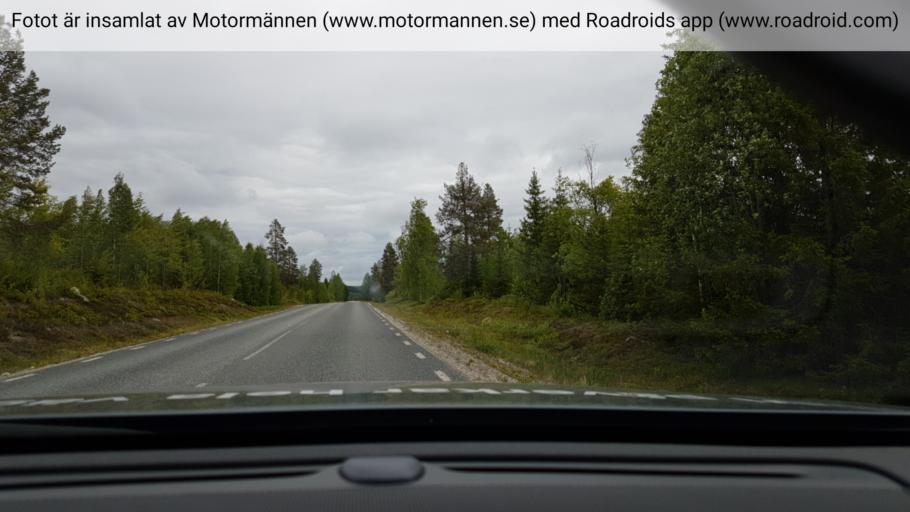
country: SE
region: Vaesterbotten
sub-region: Asele Kommun
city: Insjon
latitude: 64.3285
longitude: 17.7290
